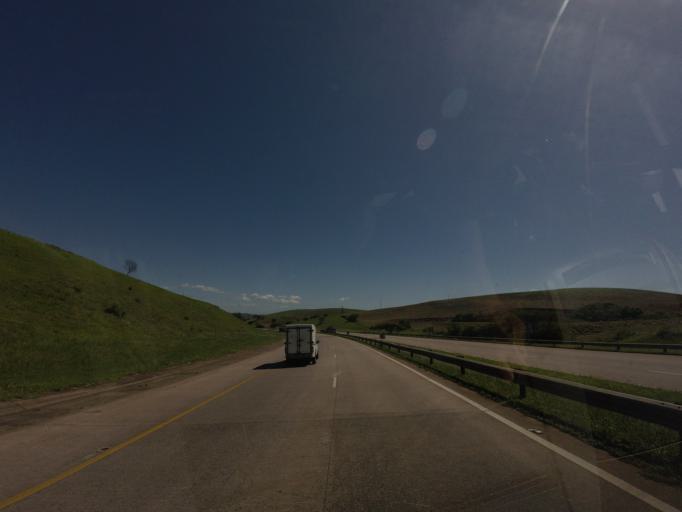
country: ZA
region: KwaZulu-Natal
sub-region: iLembe District Municipality
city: Stanger
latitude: -29.3866
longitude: 31.2974
